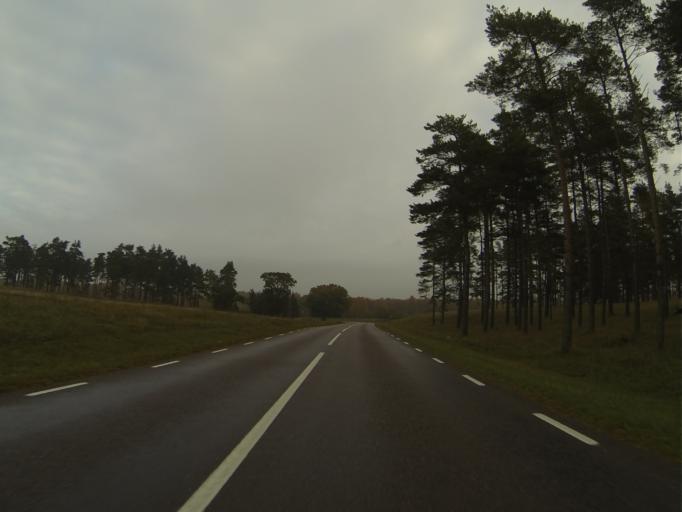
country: SE
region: Skane
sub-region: Lunds Kommun
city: Veberod
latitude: 55.6675
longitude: 13.4915
